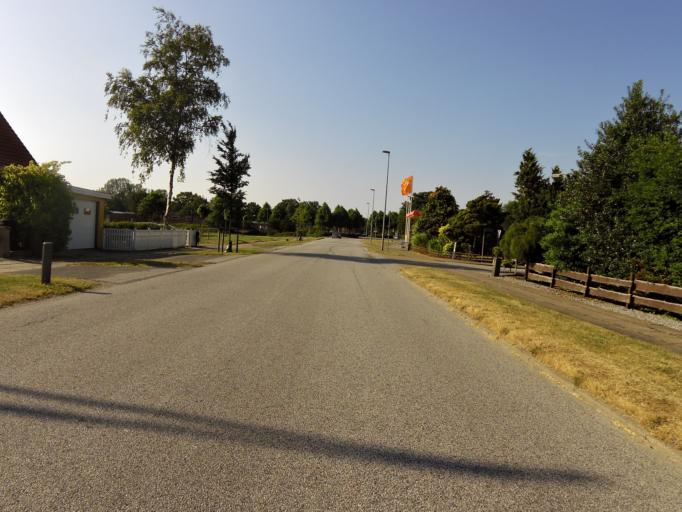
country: DK
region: South Denmark
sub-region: Haderslev Kommune
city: Vojens
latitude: 55.2430
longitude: 9.2935
